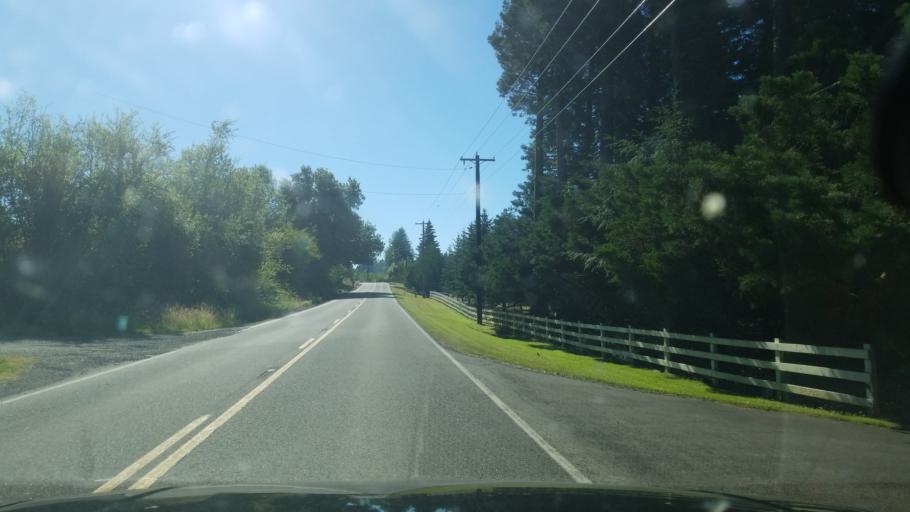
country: US
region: Oregon
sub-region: Yamhill County
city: McMinnville
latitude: 45.2255
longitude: -123.2638
